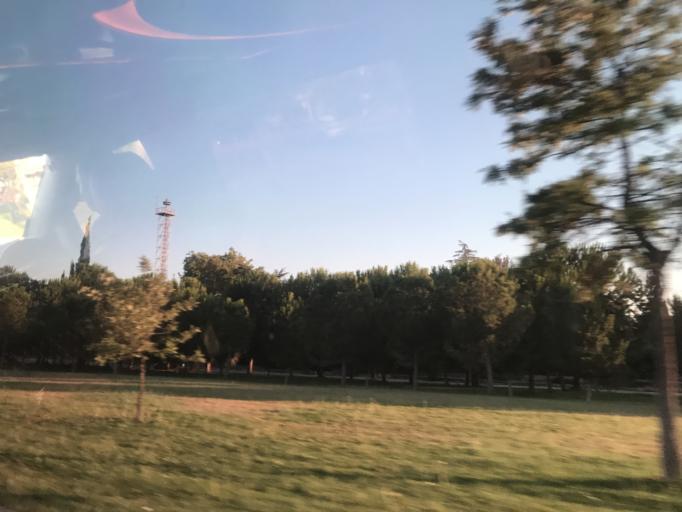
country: TR
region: Antalya
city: Antalya
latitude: 36.9349
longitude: 30.6559
